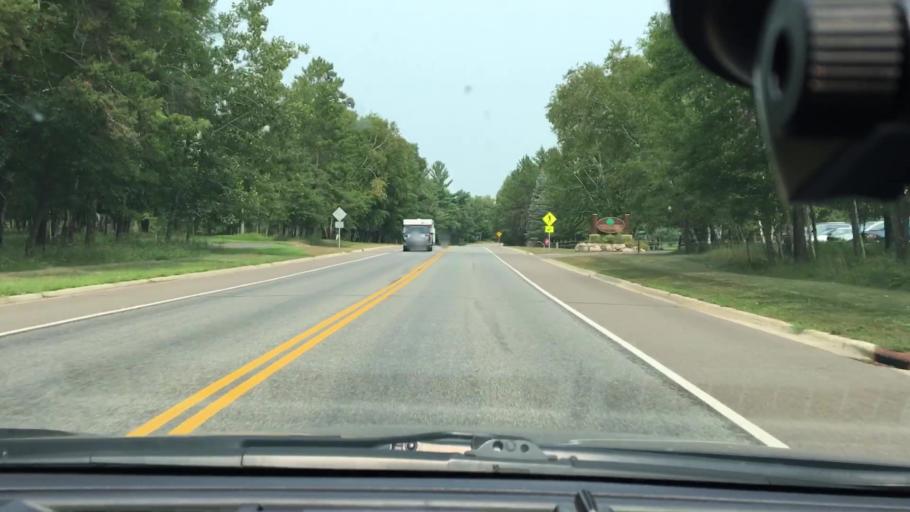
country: US
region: Minnesota
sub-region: Crow Wing County
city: Cross Lake
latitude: 46.6724
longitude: -94.0986
